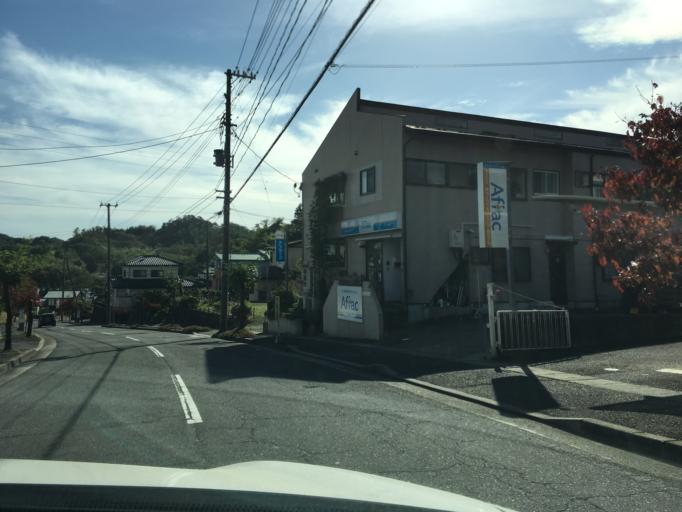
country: JP
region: Fukushima
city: Miharu
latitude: 37.4446
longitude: 140.4790
